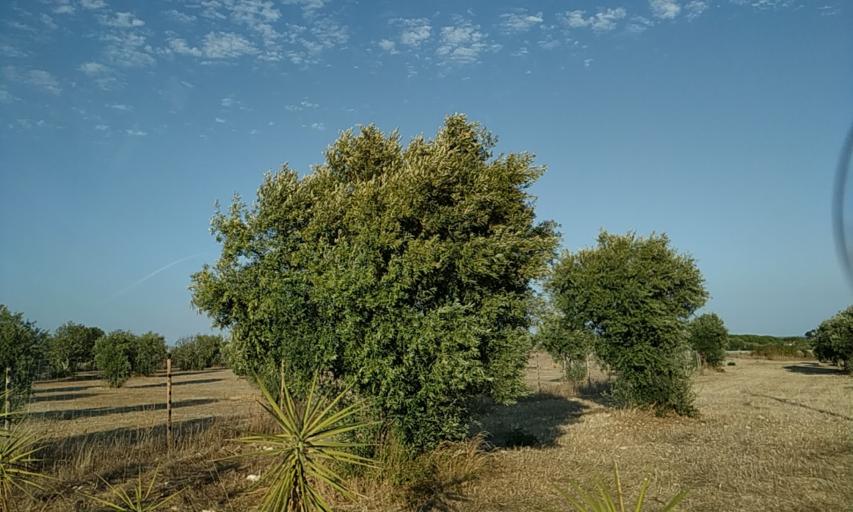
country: PT
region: Santarem
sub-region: Alcanena
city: Alcanena
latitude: 39.4100
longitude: -8.6384
